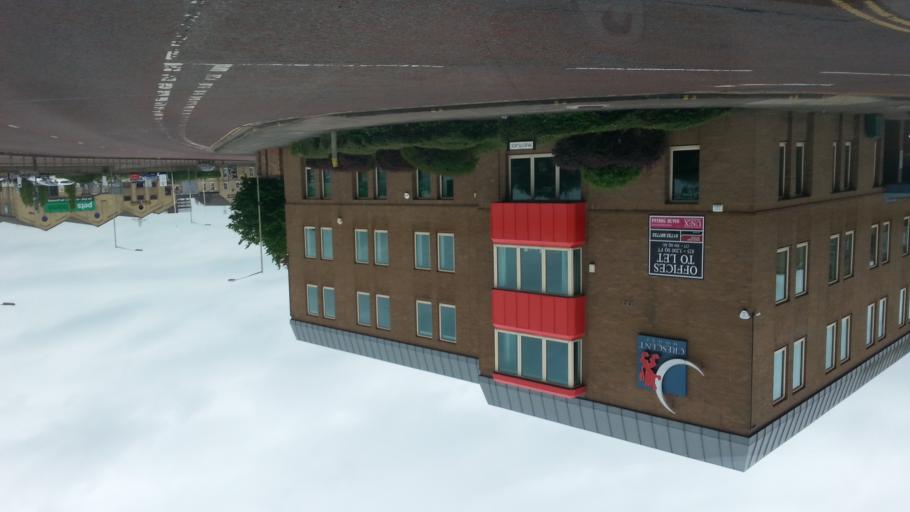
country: GB
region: England
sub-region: Peterborough
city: Peterborough
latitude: 52.5721
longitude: -0.2471
